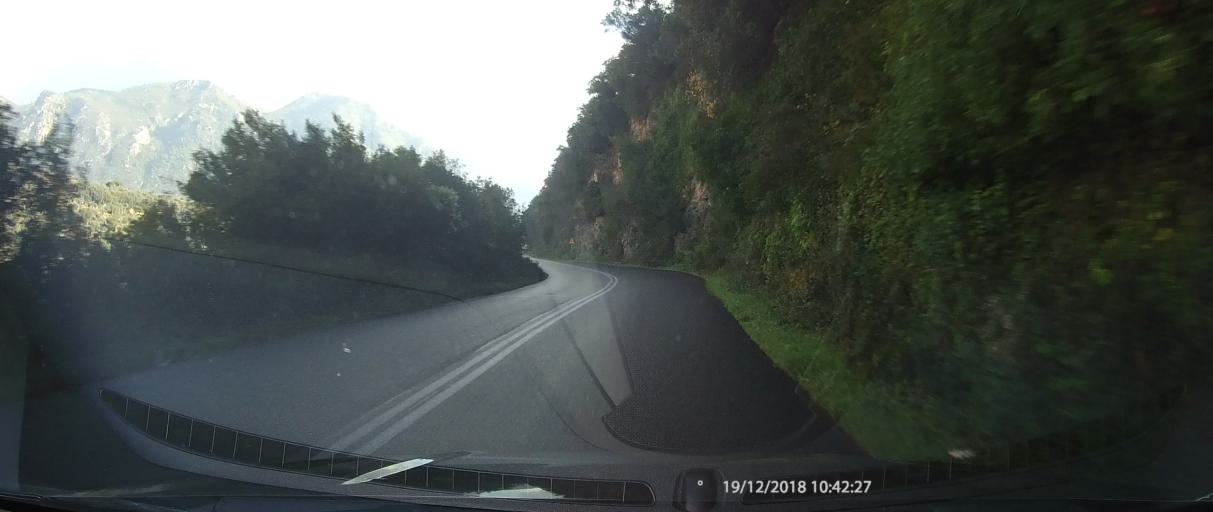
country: GR
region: Peloponnese
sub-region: Nomos Messinias
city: Paralia Vergas
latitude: 36.9537
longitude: 22.1907
